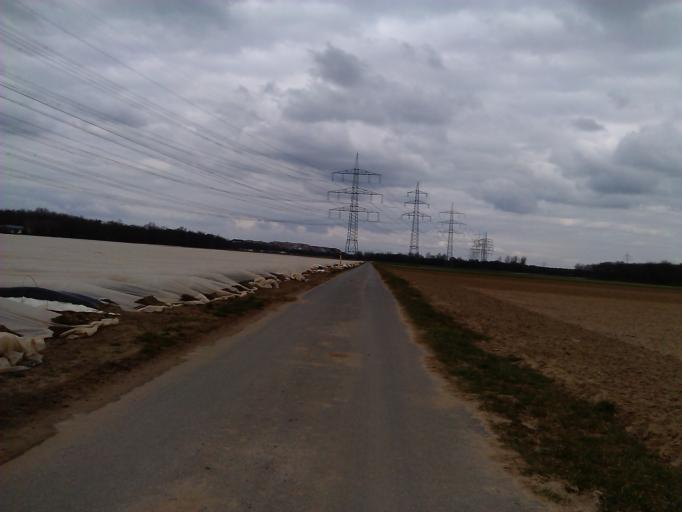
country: DE
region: Hesse
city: Griesheim
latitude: 49.8818
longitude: 8.5503
